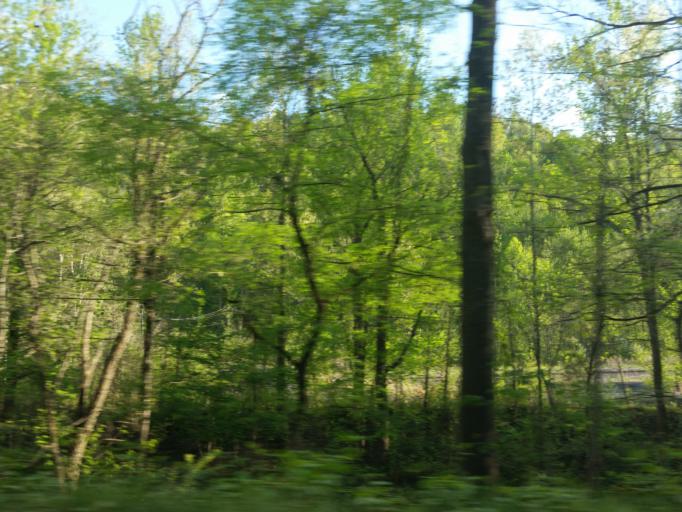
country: US
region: Kentucky
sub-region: Bell County
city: Middlesboro
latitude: 36.6146
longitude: -83.7791
